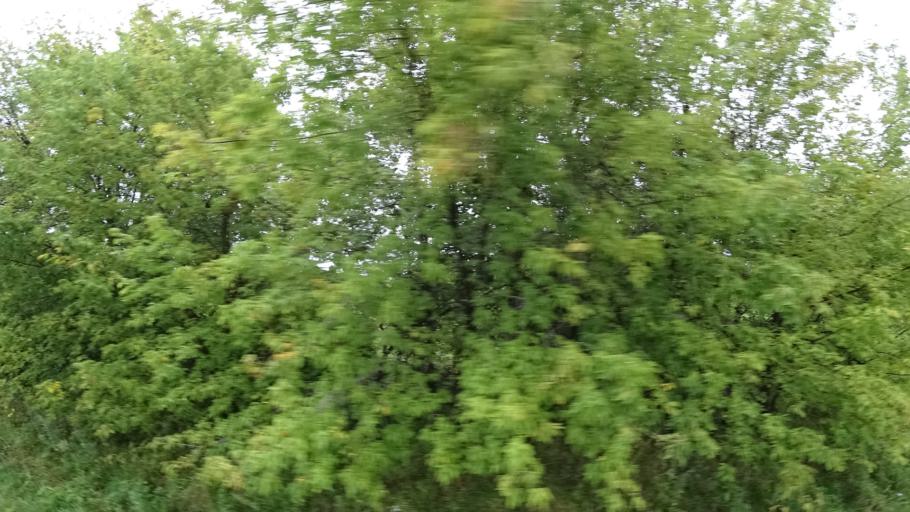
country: RU
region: Primorskiy
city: Monastyrishche
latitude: 44.2733
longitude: 132.4247
